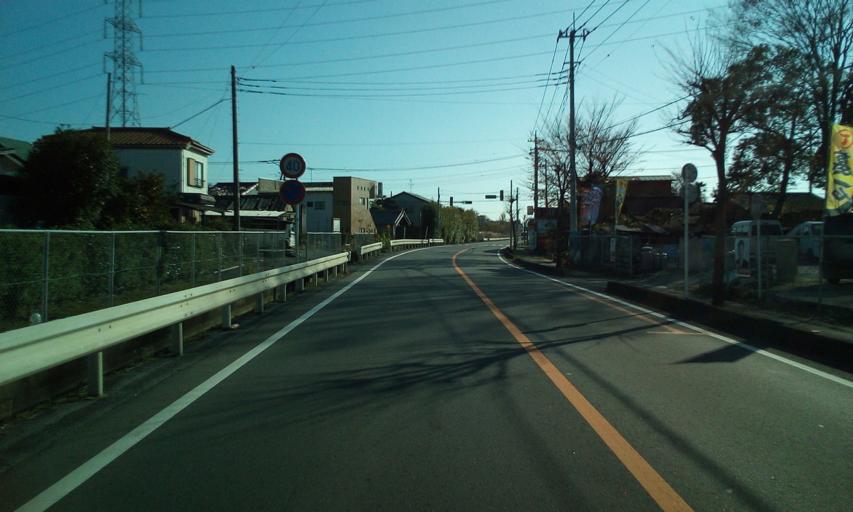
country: JP
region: Saitama
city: Kasukabe
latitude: 36.0038
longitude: 139.7953
